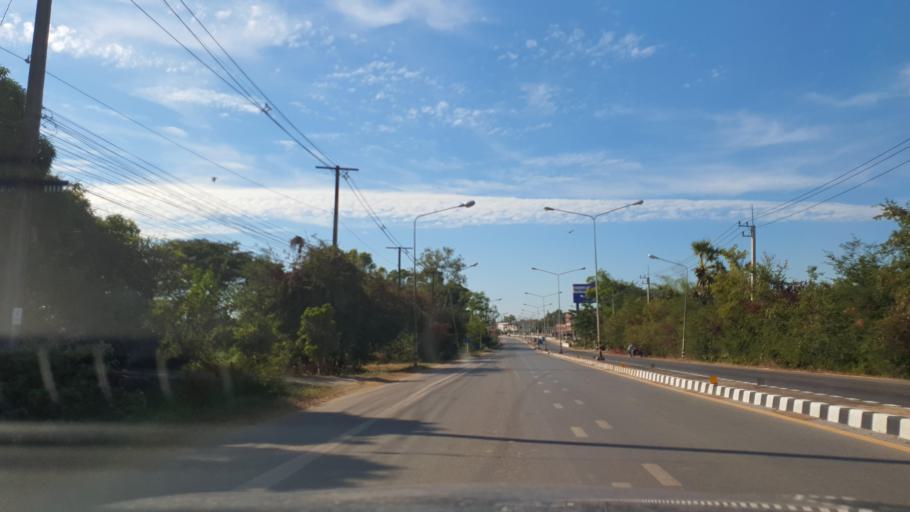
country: TH
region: Kalasin
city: Kuchinarai
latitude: 16.5364
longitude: 104.0668
